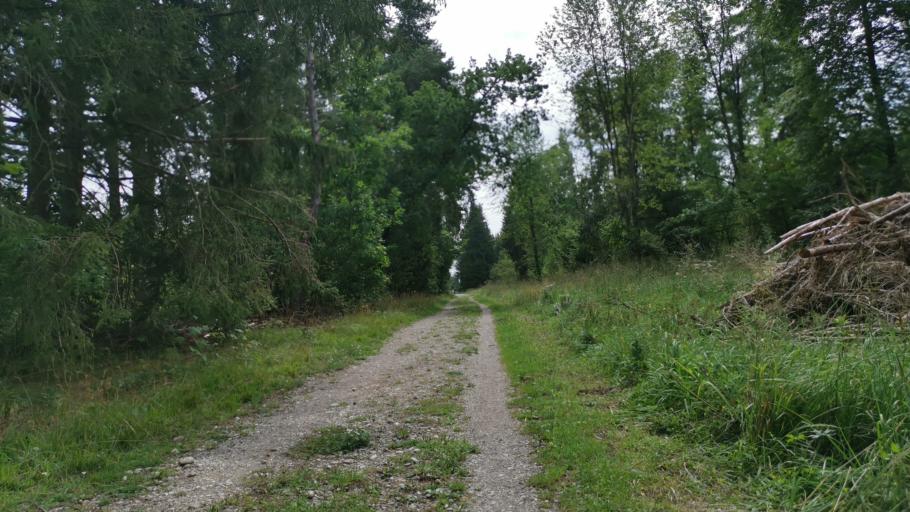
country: DE
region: Bavaria
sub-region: Upper Bavaria
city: Unterhaching
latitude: 48.0740
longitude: 11.5752
